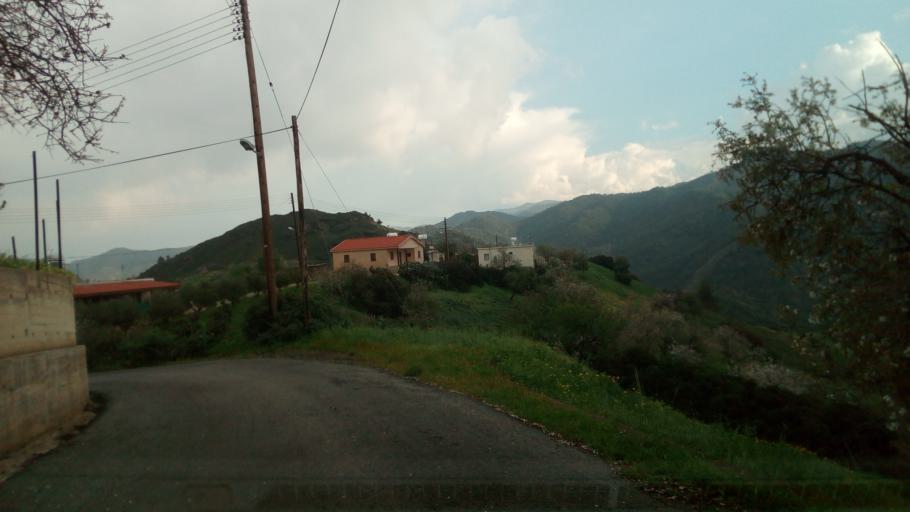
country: CY
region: Lefkosia
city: Kato Pyrgos
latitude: 35.1696
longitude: 32.6606
